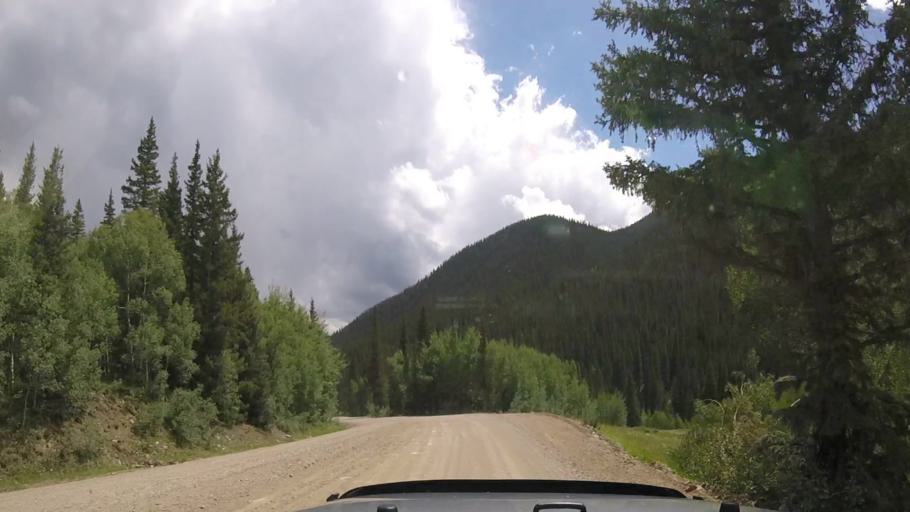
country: US
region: Colorado
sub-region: San Juan County
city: Silverton
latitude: 37.8301
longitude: -107.6707
